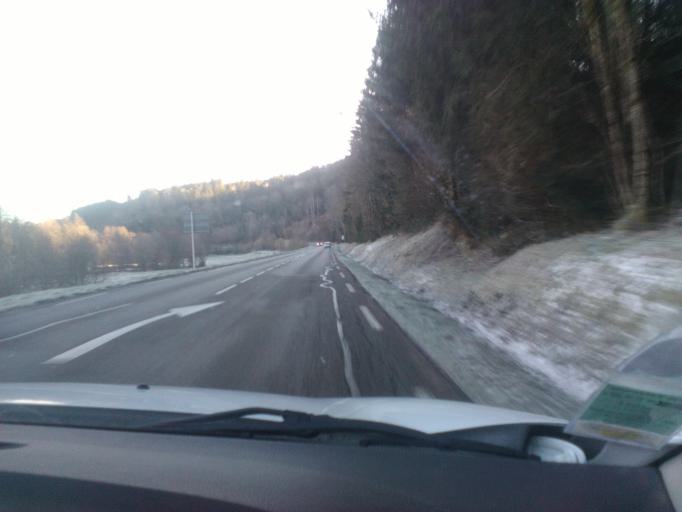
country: FR
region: Alsace
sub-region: Departement du Bas-Rhin
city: Rothau
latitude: 48.3902
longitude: 7.1479
